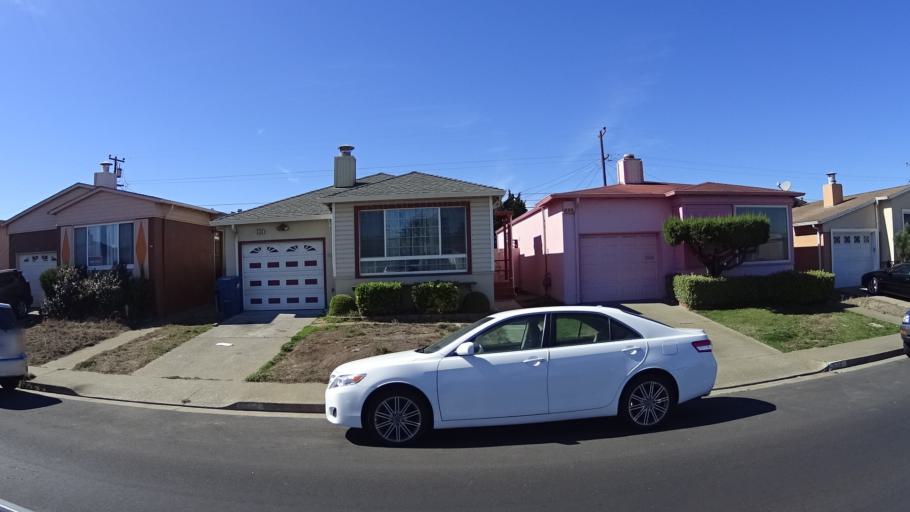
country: US
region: California
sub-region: San Mateo County
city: Broadmoor
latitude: 37.6822
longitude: -122.4903
